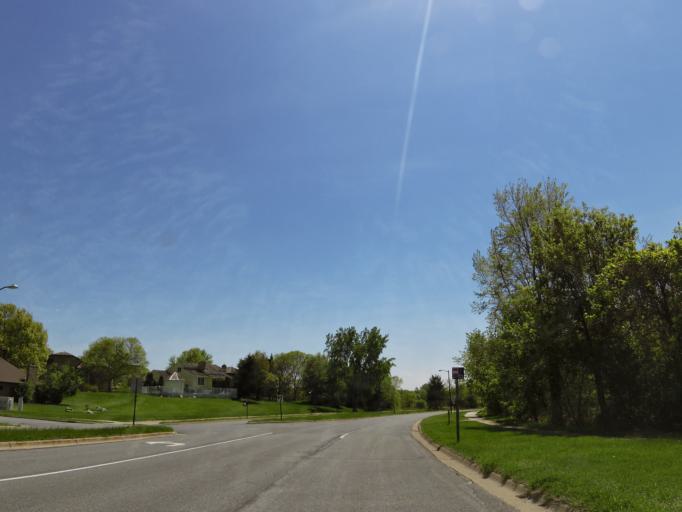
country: US
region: Minnesota
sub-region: Hennepin County
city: Edina
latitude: 44.8296
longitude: -93.3936
